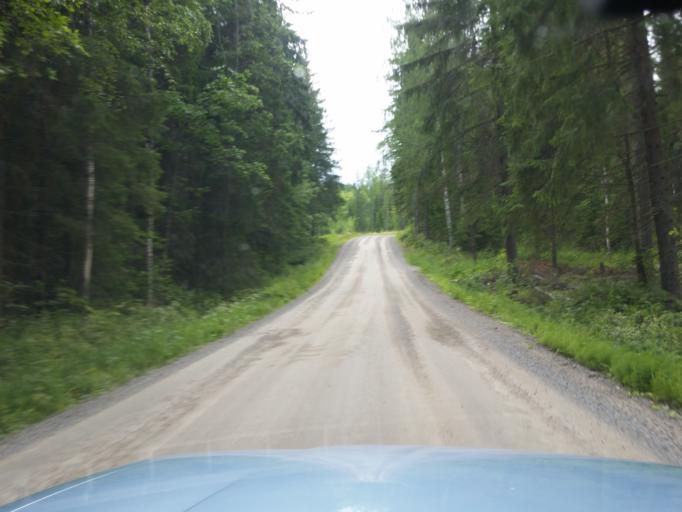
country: FI
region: Southern Savonia
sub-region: Savonlinna
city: Sulkava
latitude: 61.7391
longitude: 28.3481
